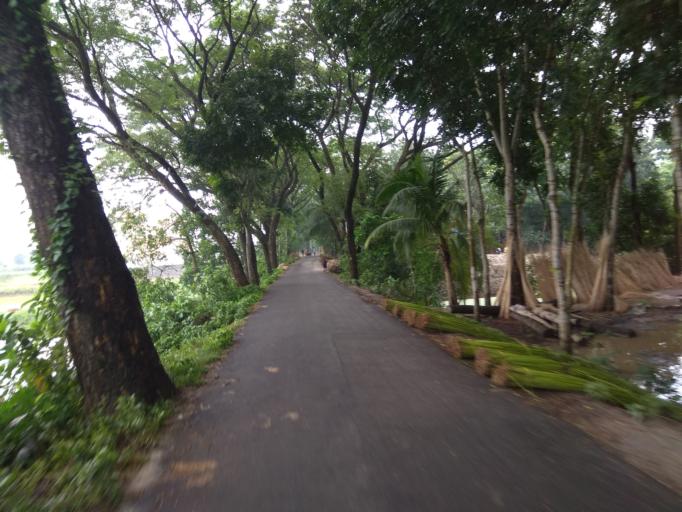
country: BD
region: Dhaka
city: Dohar
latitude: 23.4724
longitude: 90.0687
